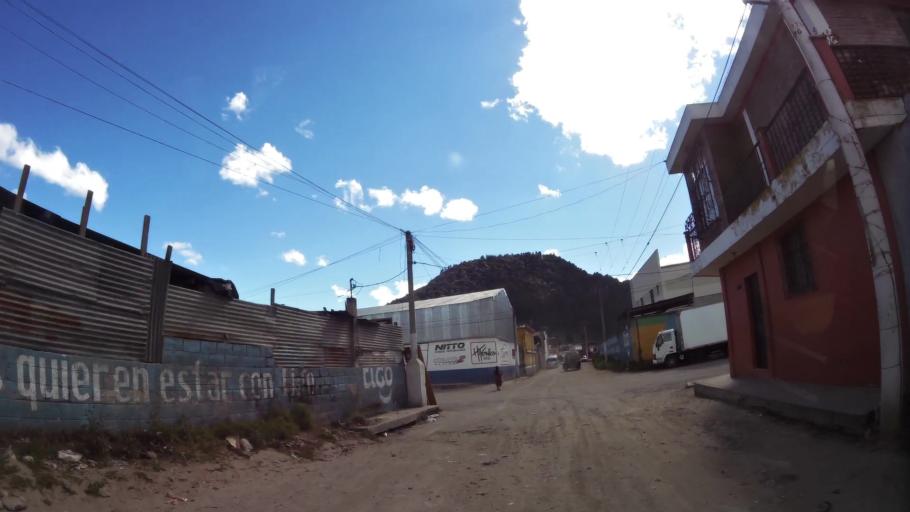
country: GT
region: Quetzaltenango
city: Quetzaltenango
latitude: 14.8359
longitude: -91.5124
